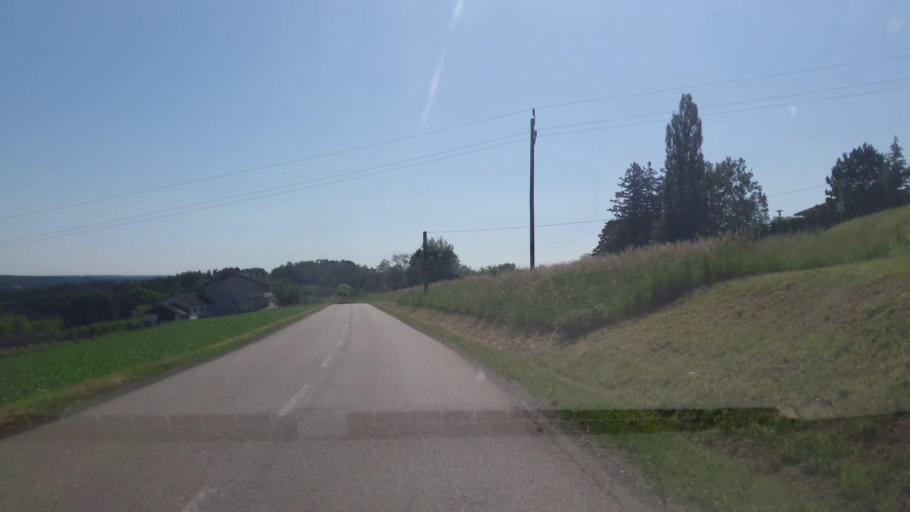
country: AT
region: Styria
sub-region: Politischer Bezirk Hartberg-Fuerstenfeld
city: Neudau
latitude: 47.1700
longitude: 16.1261
